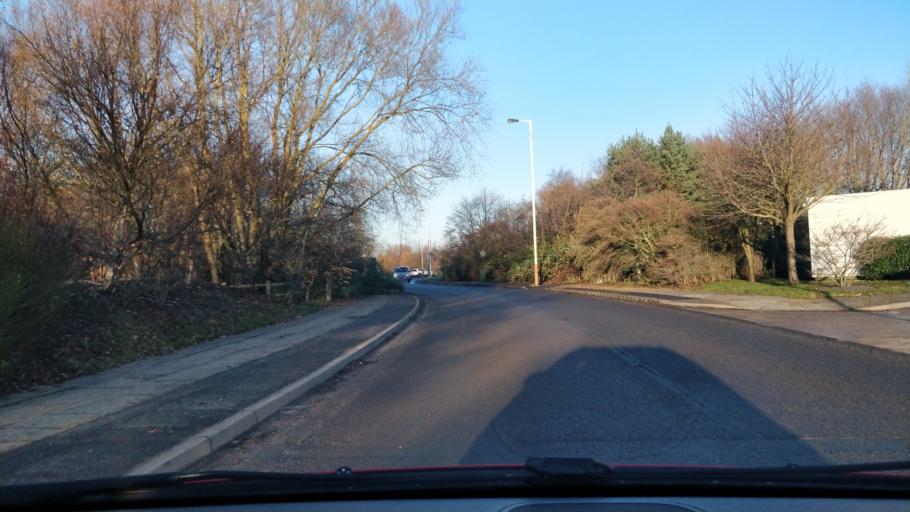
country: GB
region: England
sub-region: Sefton
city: Southport
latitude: 53.6293
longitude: -2.9880
